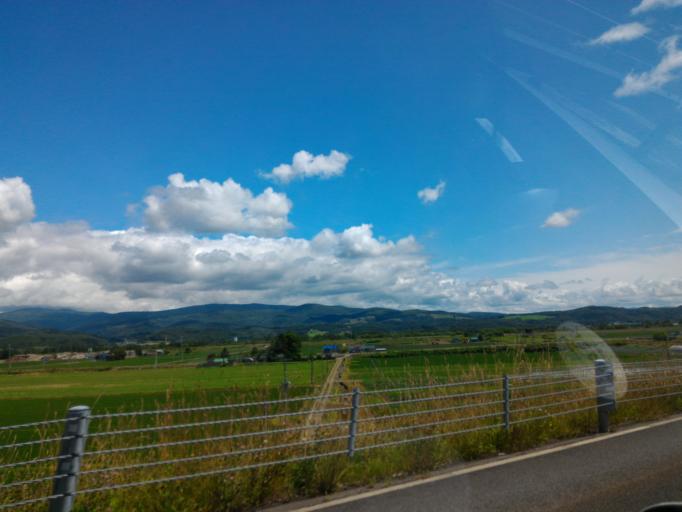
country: JP
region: Hokkaido
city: Nayoro
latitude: 44.3738
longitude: 142.4317
